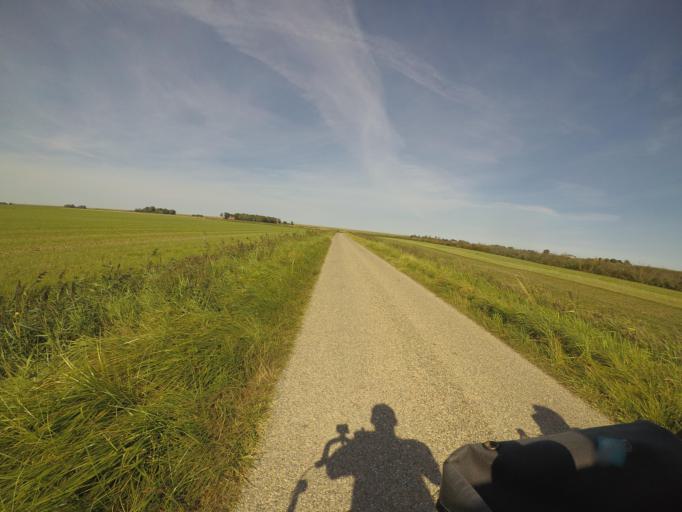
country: NL
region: Friesland
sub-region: Gemeente Ferwerderadiel
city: Ferwert
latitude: 53.3394
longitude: 5.8169
